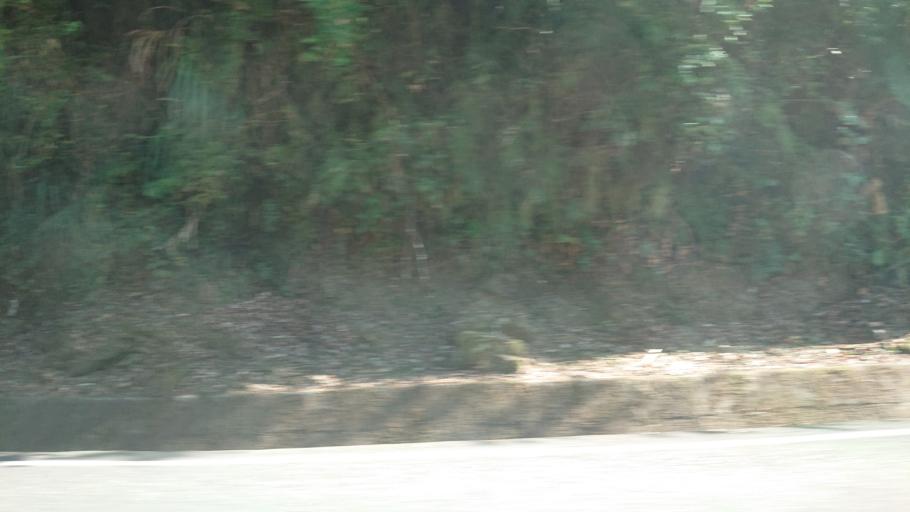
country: TW
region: Taiwan
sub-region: Chiayi
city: Jiayi Shi
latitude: 23.4635
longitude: 120.7186
